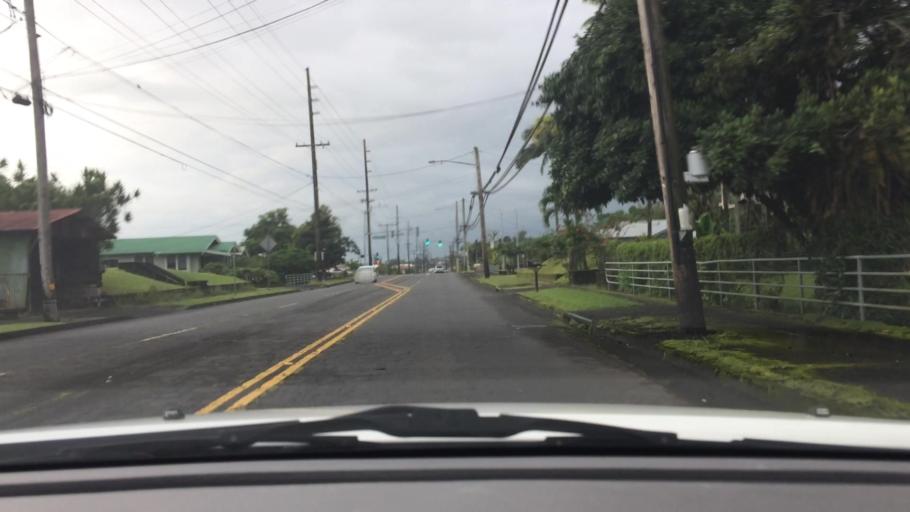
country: US
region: Hawaii
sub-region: Hawaii County
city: Hilo
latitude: 19.7103
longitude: -155.0796
